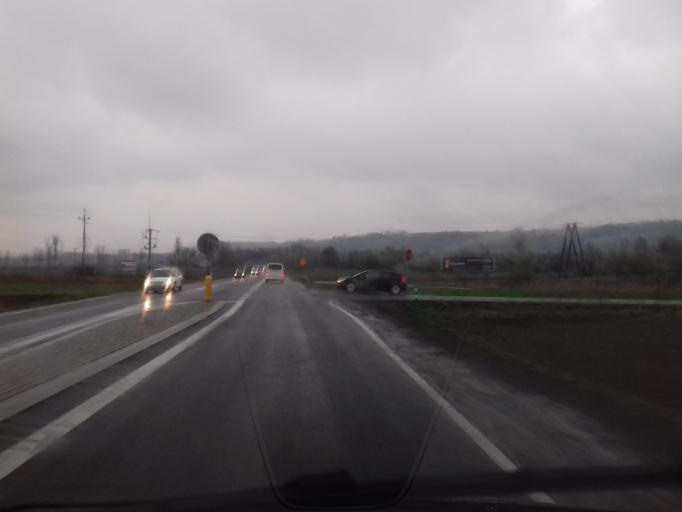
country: PL
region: Lesser Poland Voivodeship
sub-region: Powiat nowosadecki
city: Stary Sacz
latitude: 49.5470
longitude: 20.6513
